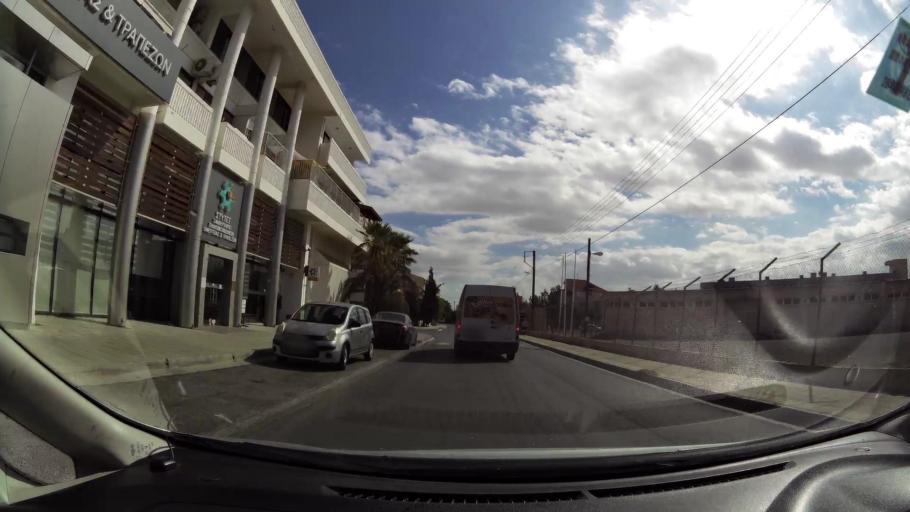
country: CY
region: Lefkosia
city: Nicosia
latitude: 35.1453
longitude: 33.3699
